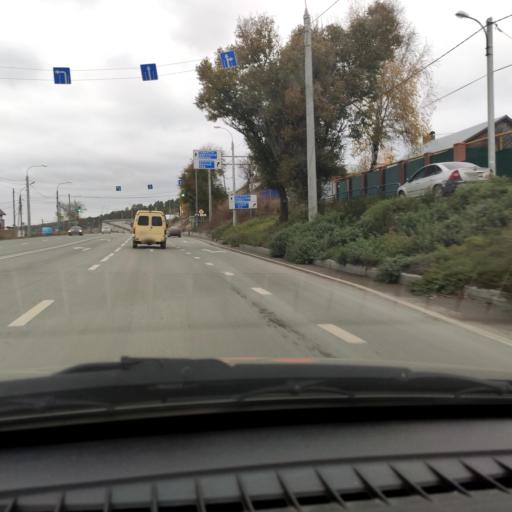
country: RU
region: Samara
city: Volzhskiy
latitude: 53.4302
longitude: 50.1188
